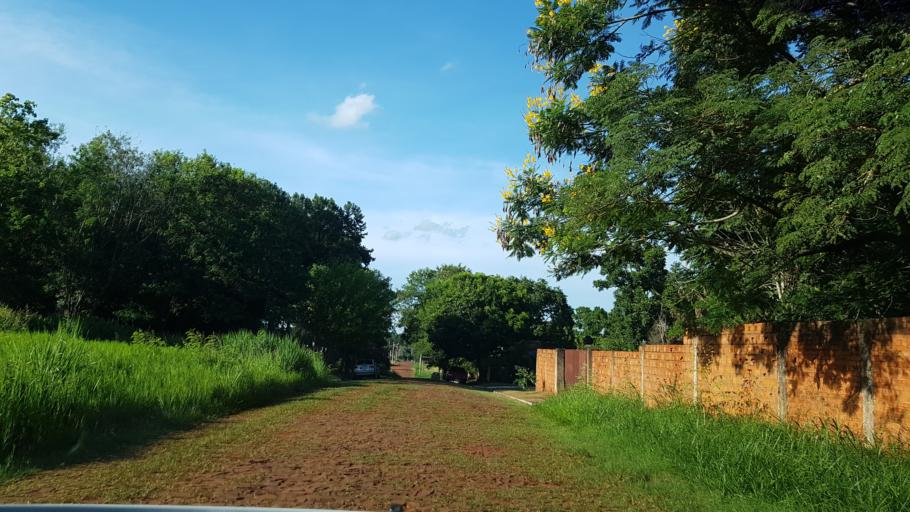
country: AR
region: Misiones
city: Puerto Libertad
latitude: -25.9226
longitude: -54.5898
